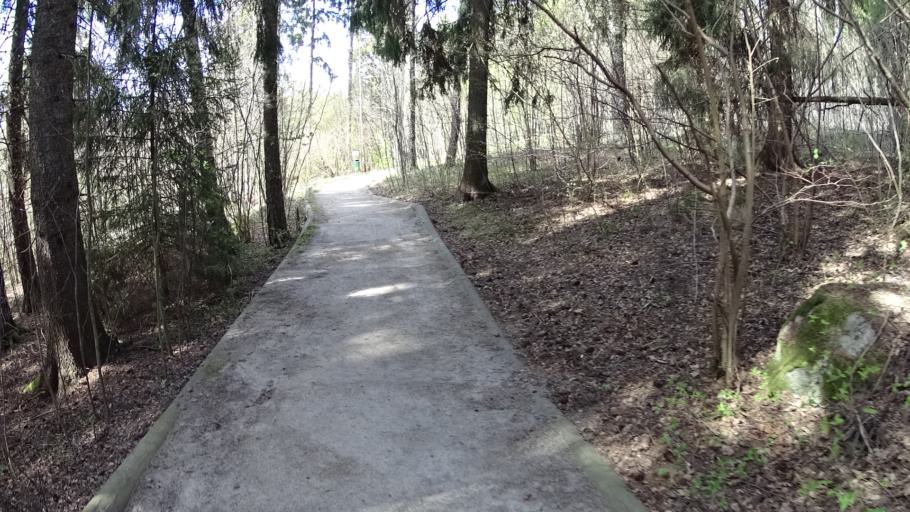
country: FI
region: Uusimaa
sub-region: Helsinki
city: Siuntio
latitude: 60.1668
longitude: 24.2146
